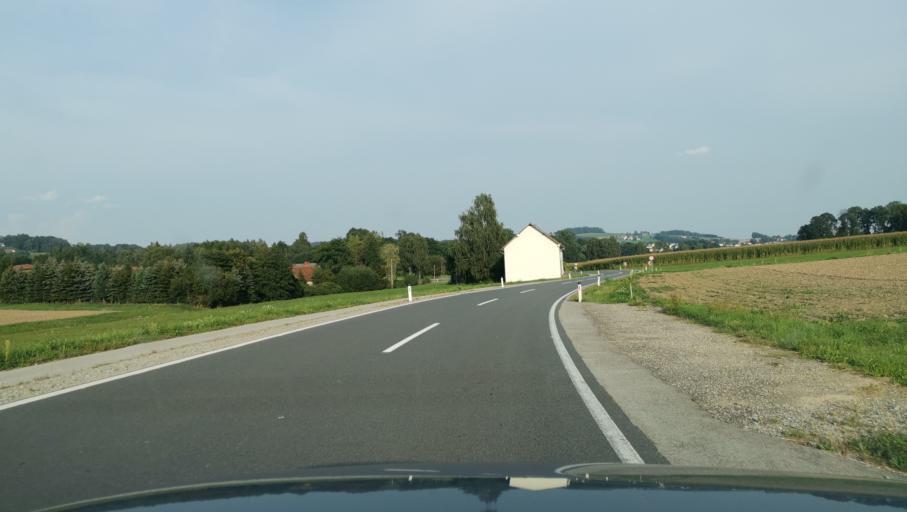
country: AT
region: Upper Austria
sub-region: Politischer Bezirk Grieskirchen
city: Grieskirchen
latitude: 48.3473
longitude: 13.7450
